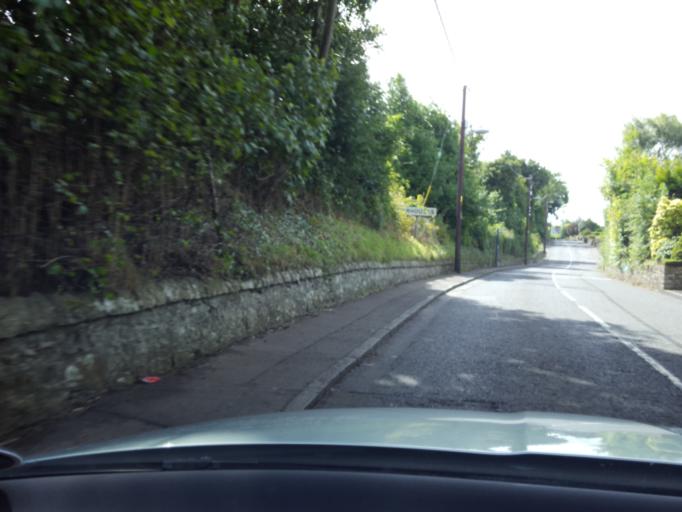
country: GB
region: Scotland
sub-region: Falkirk
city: Bo'ness
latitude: 56.0109
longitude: -3.5756
